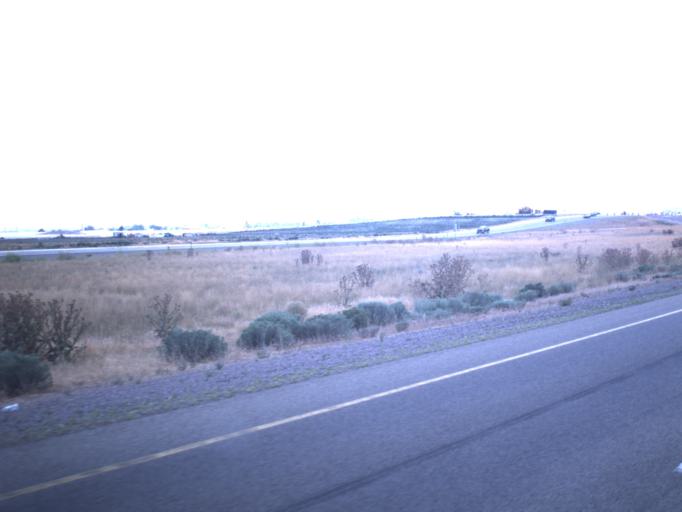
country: US
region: Utah
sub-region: Salt Lake County
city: Herriman
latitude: 40.5152
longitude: -112.0058
